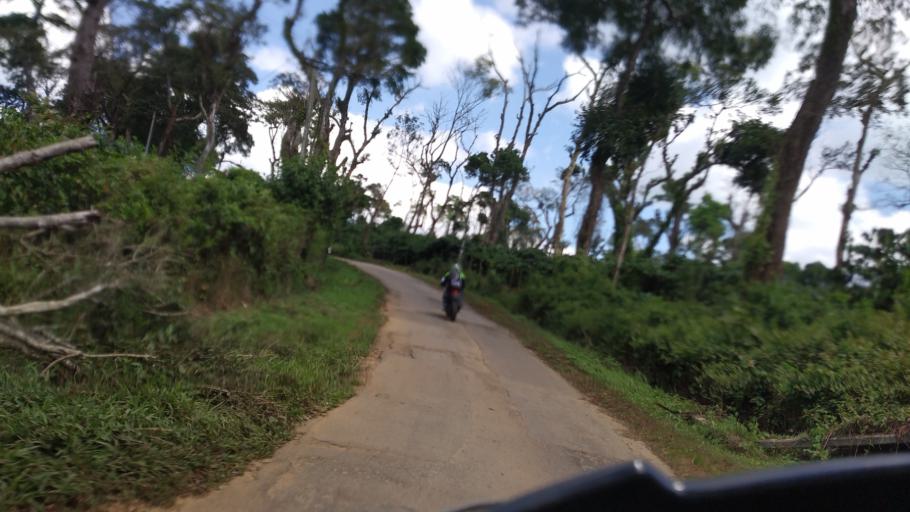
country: IN
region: Karnataka
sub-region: Kodagu
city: Ponnampet
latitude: 12.0245
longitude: 75.8921
